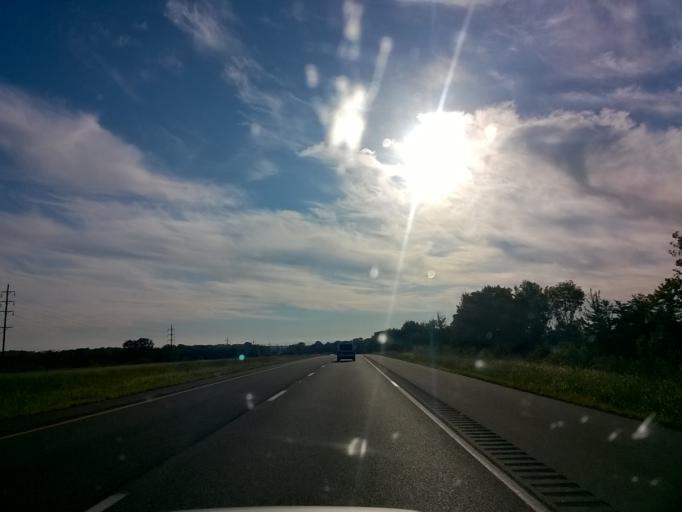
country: US
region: Indiana
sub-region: Warrick County
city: Boonville
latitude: 38.1993
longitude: -87.2629
